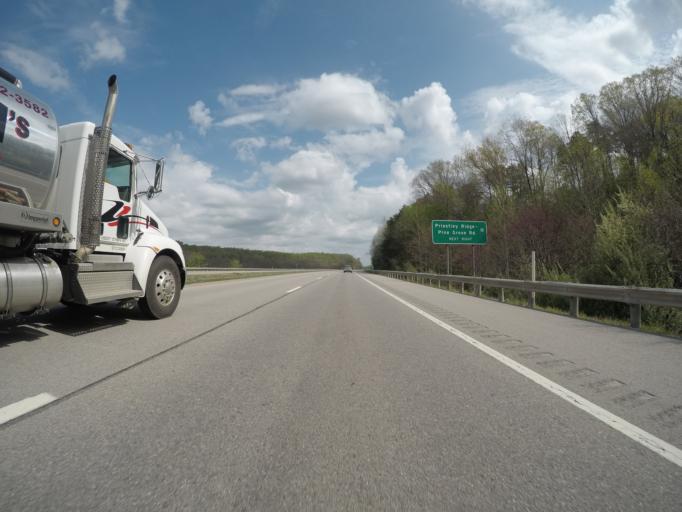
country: US
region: West Virginia
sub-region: Kanawha County
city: Alum Creek
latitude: 38.2385
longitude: -81.8393
